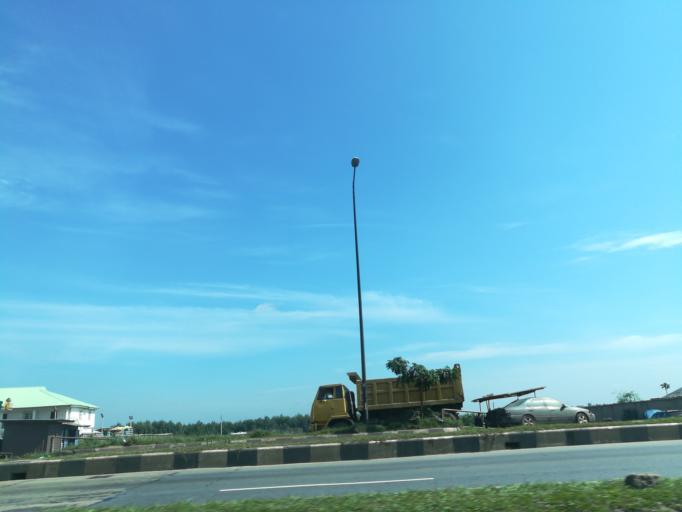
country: NG
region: Lagos
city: Ebute Ikorodu
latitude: 6.6193
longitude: 3.4646
